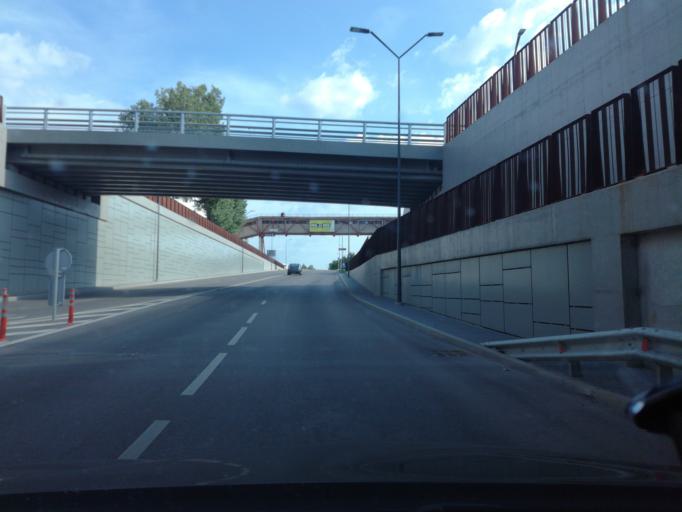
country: LT
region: Marijampoles apskritis
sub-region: Marijampole Municipality
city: Marijampole
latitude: 54.5381
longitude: 23.3508
